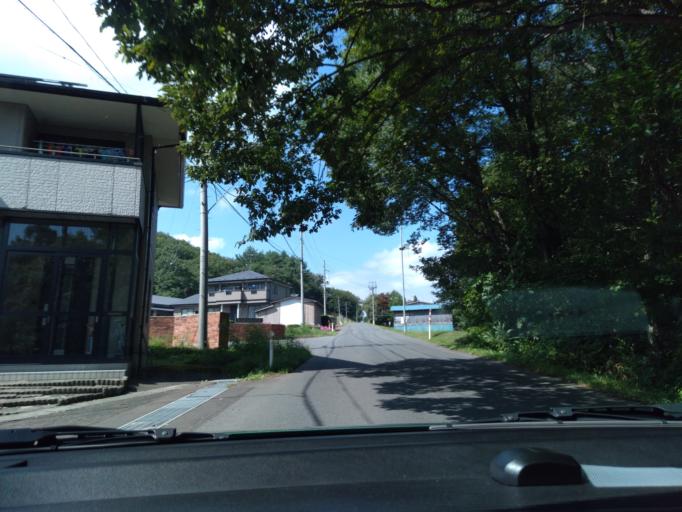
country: JP
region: Iwate
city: Shizukuishi
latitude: 39.6687
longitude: 140.9693
